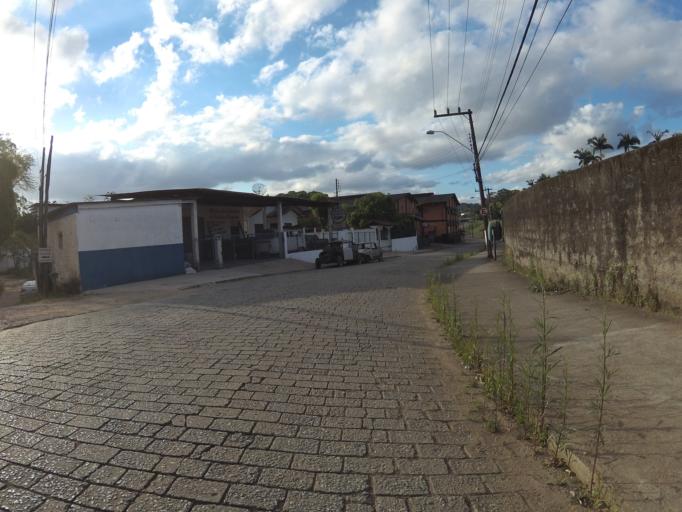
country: BR
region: Santa Catarina
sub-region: Blumenau
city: Blumenau
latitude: -26.8740
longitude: -49.0949
